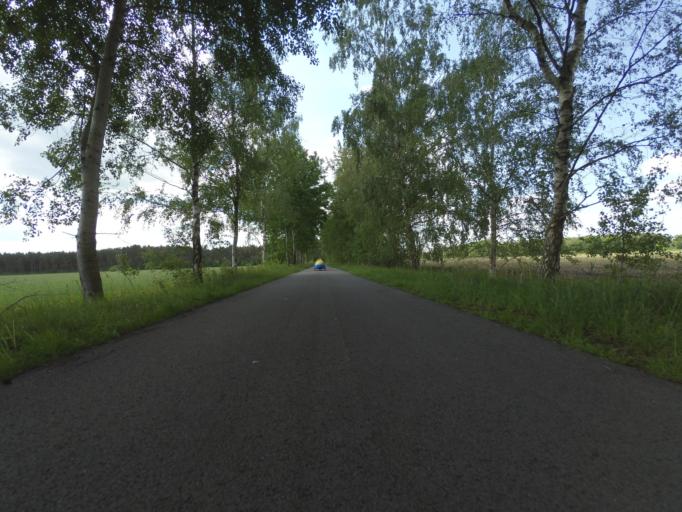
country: DE
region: Lower Saxony
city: Hohne
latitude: 52.6161
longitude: 10.3548
